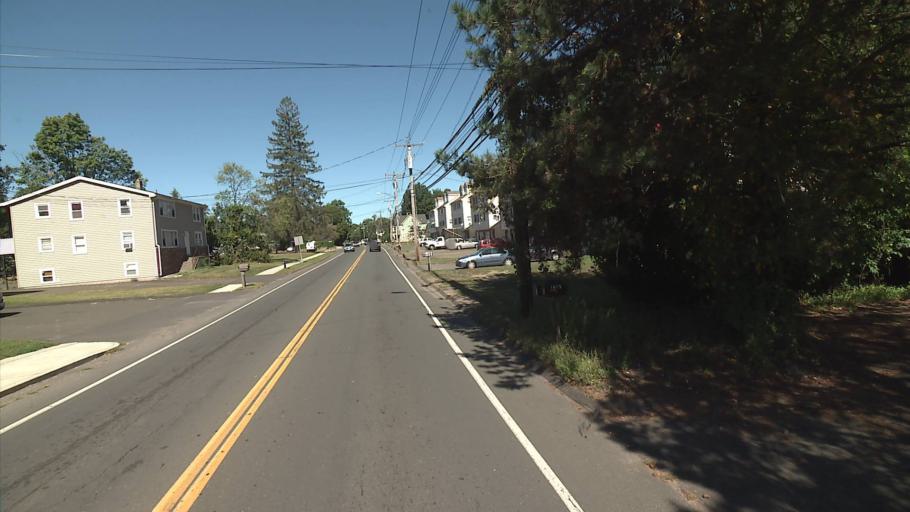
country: US
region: Connecticut
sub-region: New Haven County
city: Woodbridge
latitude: 41.3418
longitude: -72.9780
